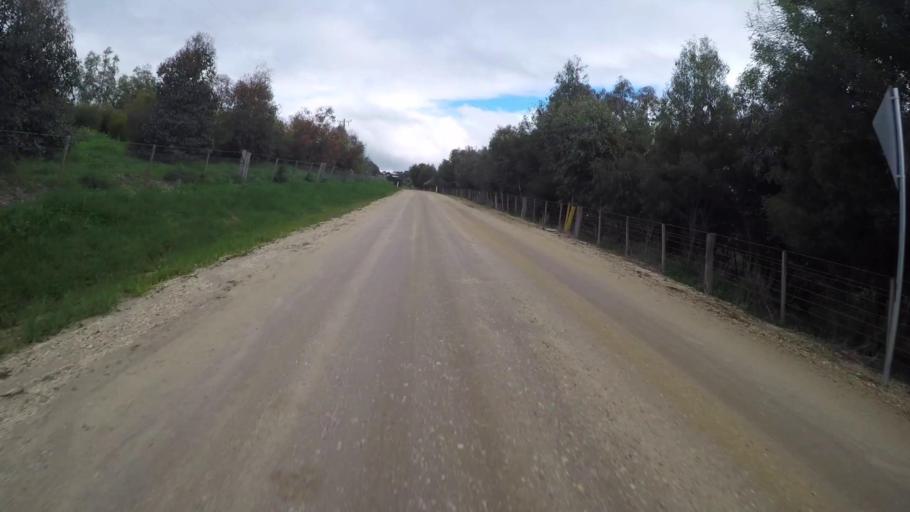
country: AU
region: Victoria
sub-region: Greater Geelong
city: Wandana Heights
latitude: -38.1718
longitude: 144.2375
